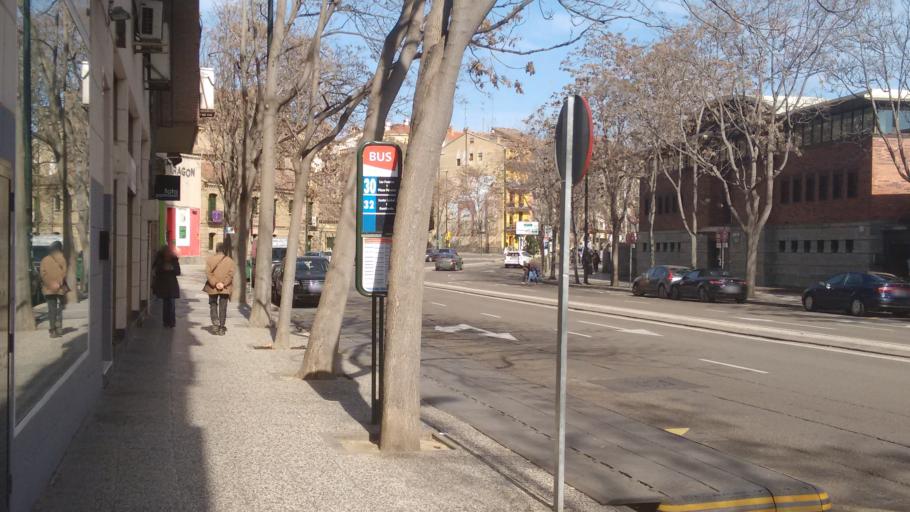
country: ES
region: Aragon
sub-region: Provincia de Zaragoza
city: Zaragoza
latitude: 41.6469
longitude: -0.8772
